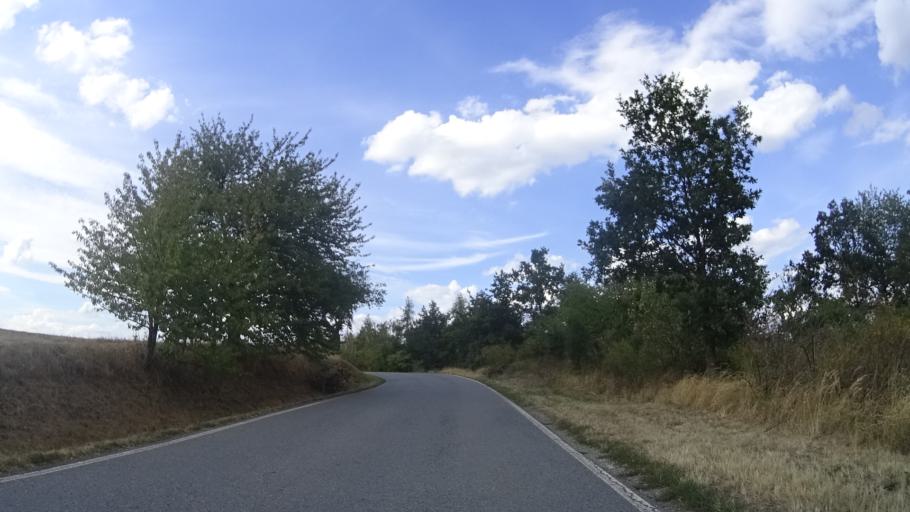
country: CZ
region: Olomoucky
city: Bila Lhota
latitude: 49.7313
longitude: 16.9801
